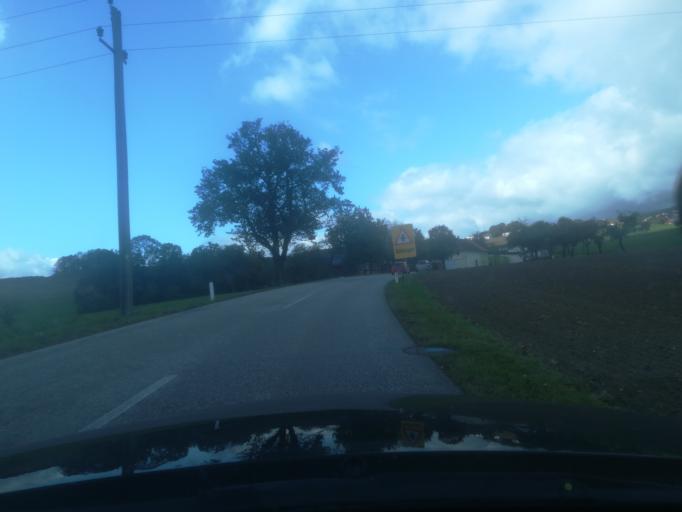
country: AT
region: Upper Austria
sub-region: Linz Stadt
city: Linz
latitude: 48.3494
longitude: 14.2656
